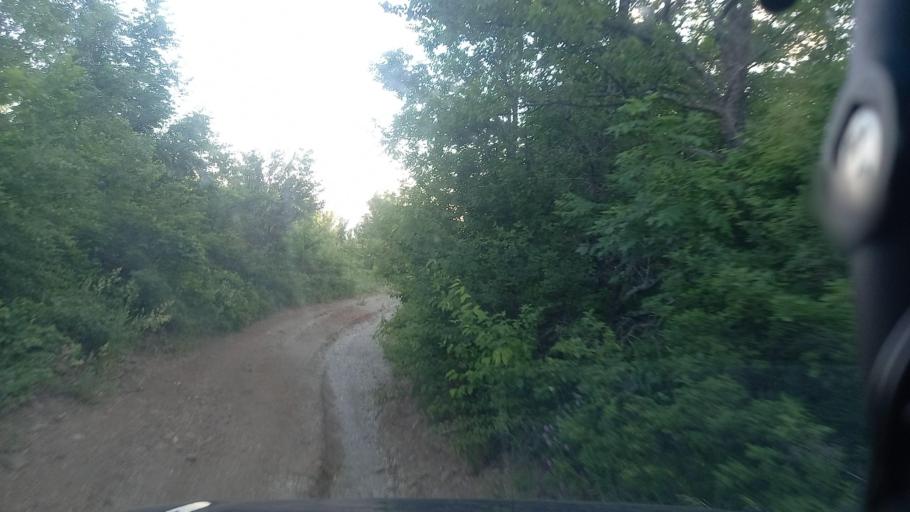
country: RU
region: Krasnodarskiy
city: Pshada
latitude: 44.5947
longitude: 38.2835
